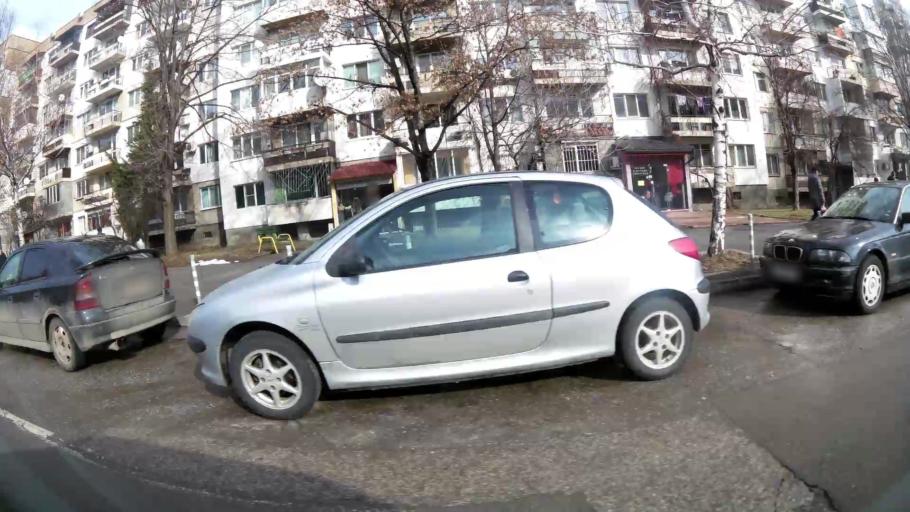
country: BG
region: Sofiya
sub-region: Obshtina Bozhurishte
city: Bozhurishte
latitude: 42.7176
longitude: 23.2483
